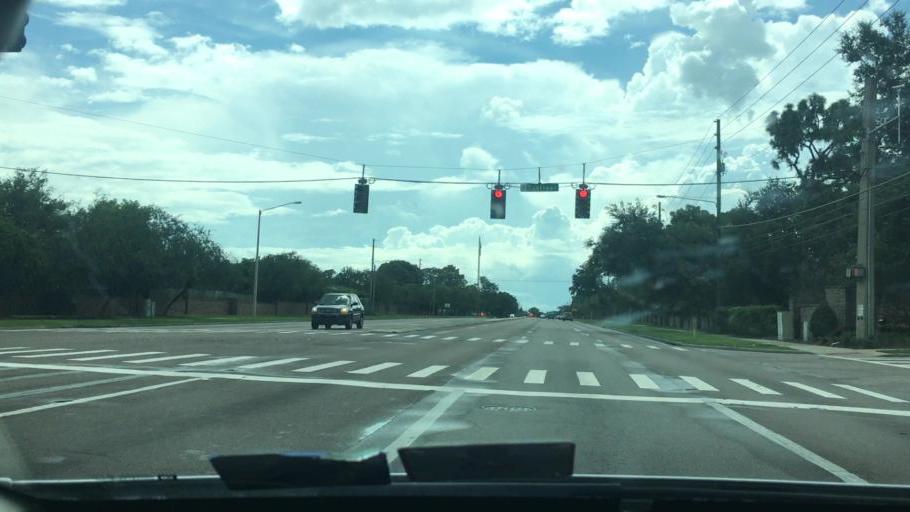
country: US
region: Florida
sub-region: Orange County
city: Alafaya
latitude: 28.5976
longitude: -81.2356
